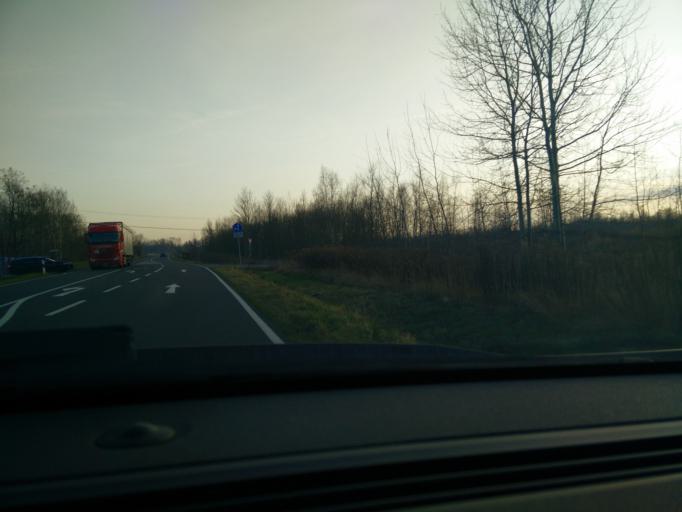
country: DE
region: Saxony
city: Espenhain
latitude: 51.2043
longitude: 12.4547
